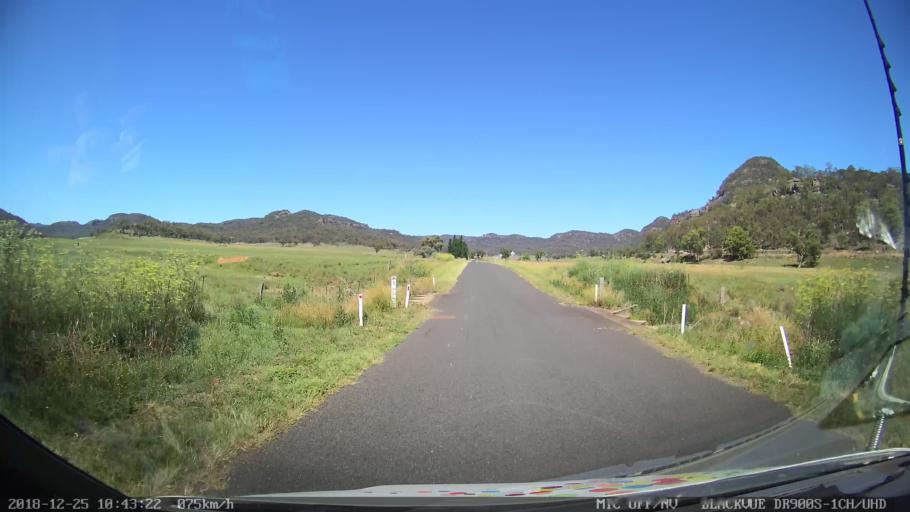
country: AU
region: New South Wales
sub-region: Upper Hunter Shire
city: Merriwa
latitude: -32.4218
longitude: 150.3137
